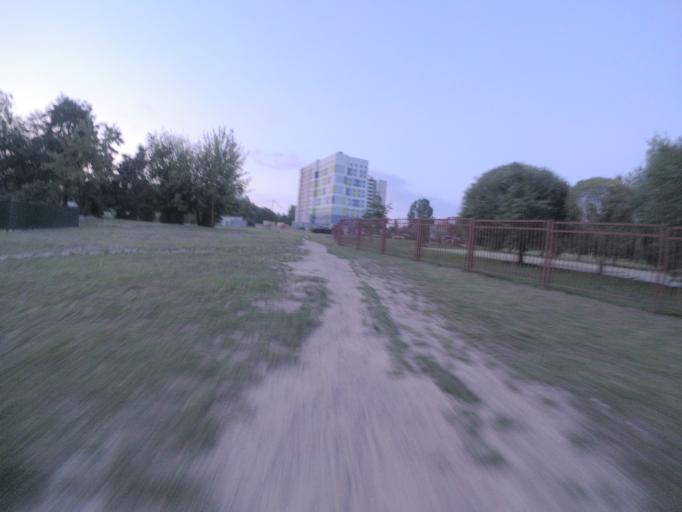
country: BY
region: Grodnenskaya
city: Hrodna
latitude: 53.7016
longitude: 23.8107
